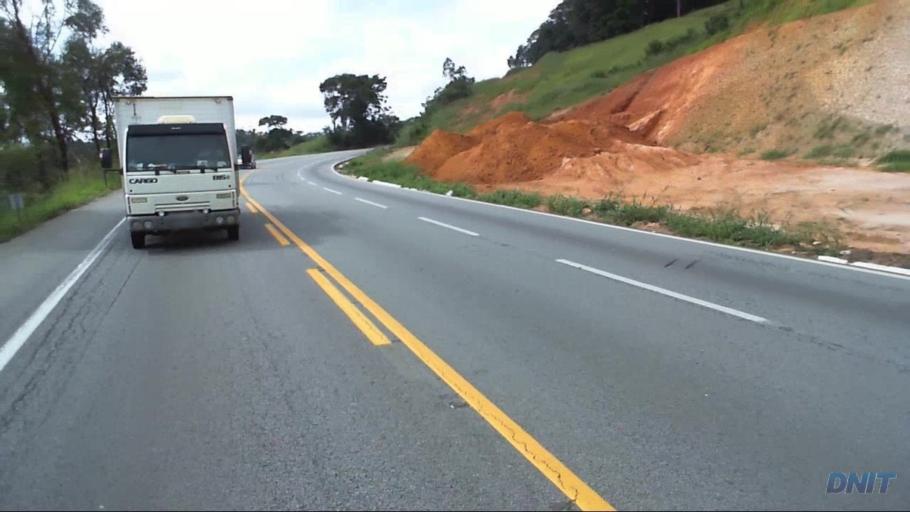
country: BR
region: Minas Gerais
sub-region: Caete
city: Caete
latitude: -19.7424
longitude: -43.6136
